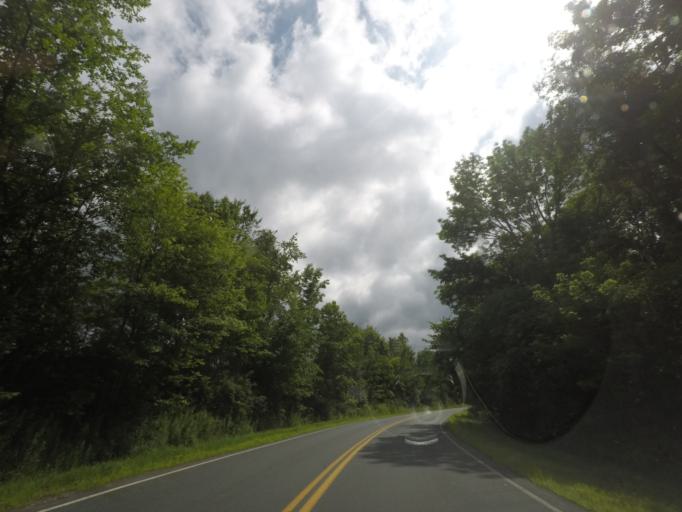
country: US
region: New York
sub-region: Saratoga County
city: Stillwater
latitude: 42.8869
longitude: -73.5606
